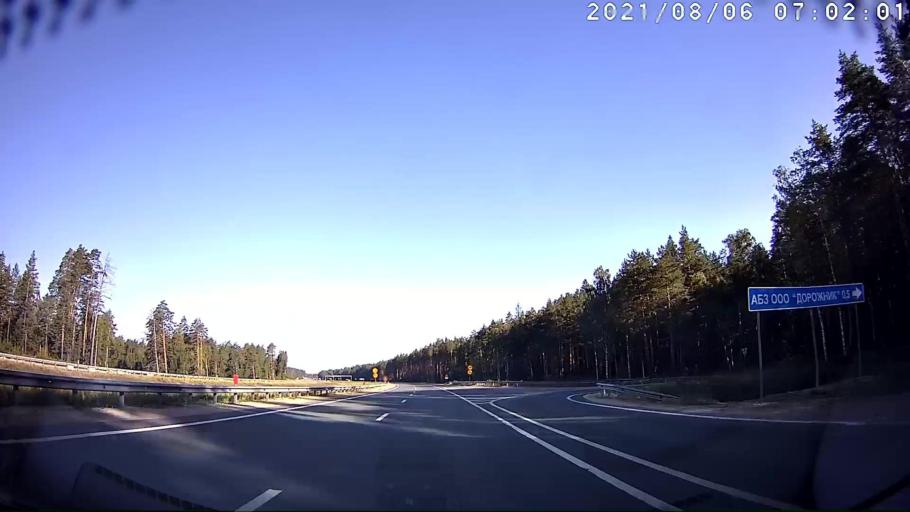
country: RU
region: Mariy-El
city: Surok
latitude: 56.5299
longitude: 48.0030
